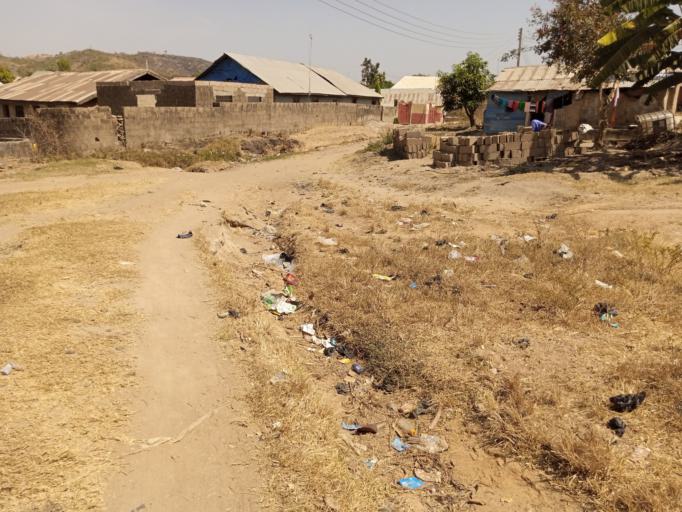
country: NG
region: Abuja Federal Capital Territory
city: Kuje
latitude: 8.9028
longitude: 7.3412
